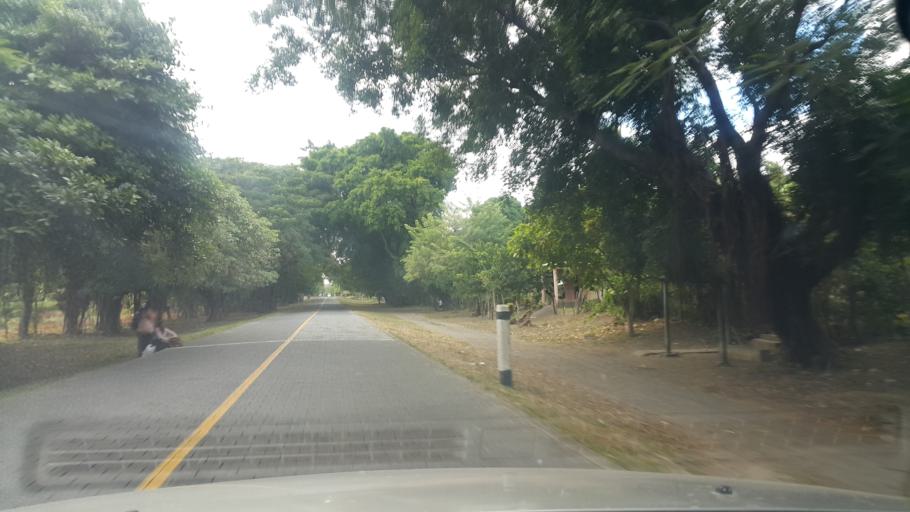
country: NI
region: Rivas
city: Moyogalpa
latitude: 11.4904
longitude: -85.6620
